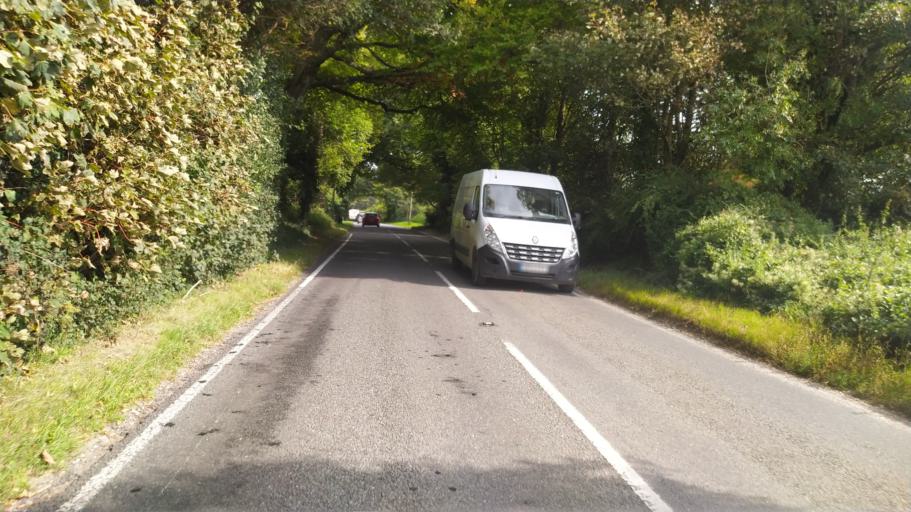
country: GB
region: England
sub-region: Dorset
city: Three Legged Cross
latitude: 50.8951
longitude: -1.9503
